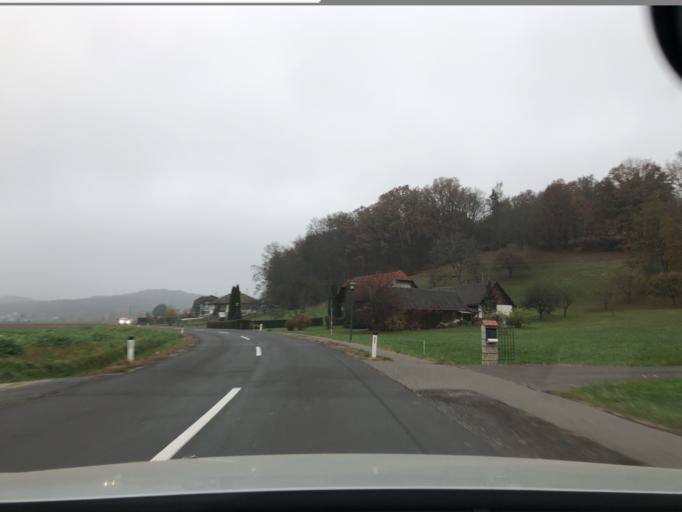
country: AT
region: Styria
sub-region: Politischer Bezirk Suedoststeiermark
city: Fehring
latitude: 46.9564
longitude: 16.0310
